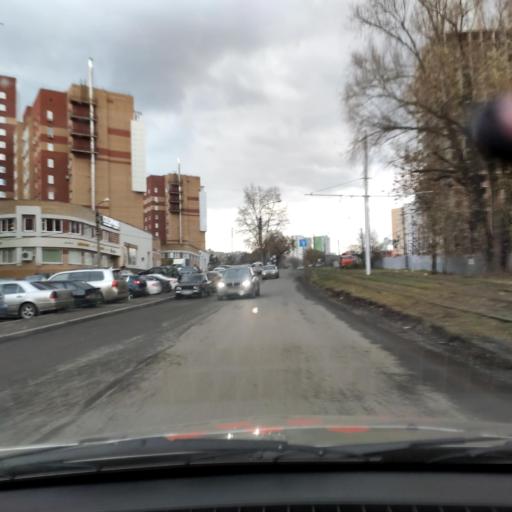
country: RU
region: Bashkortostan
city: Ufa
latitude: 54.7152
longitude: 55.9745
